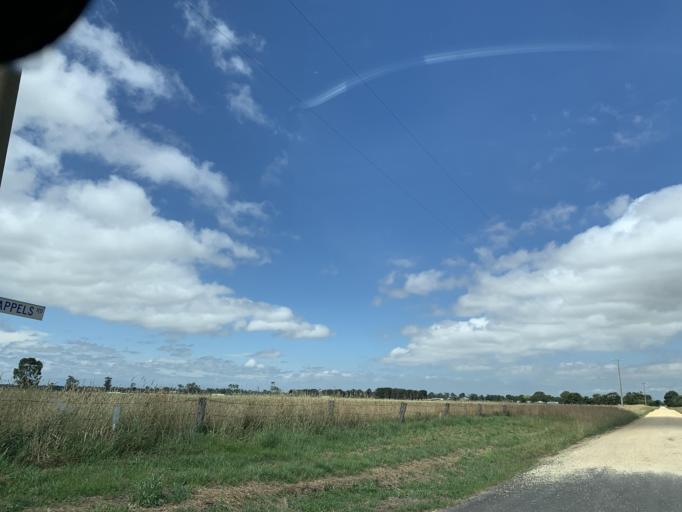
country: AU
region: Victoria
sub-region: Latrobe
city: Traralgon
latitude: -38.0911
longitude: 146.5815
